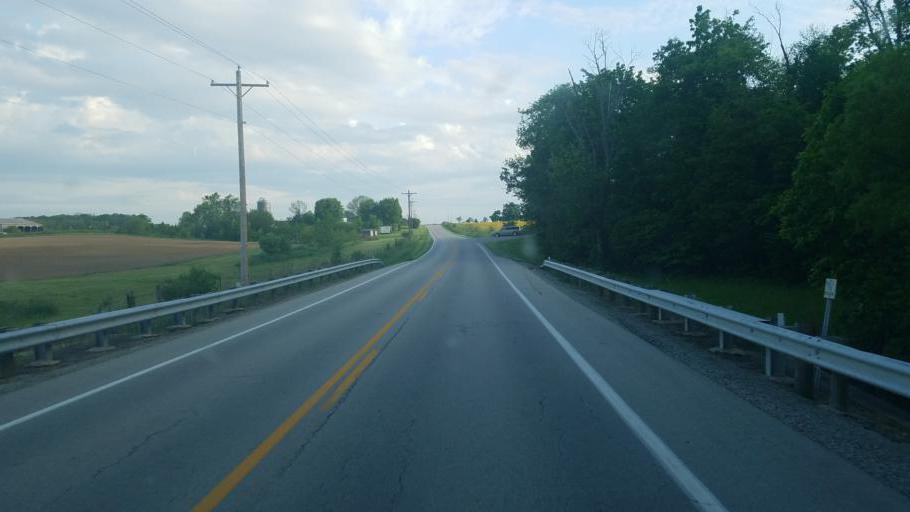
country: US
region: Ohio
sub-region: Highland County
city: Leesburg
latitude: 39.3919
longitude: -83.5959
